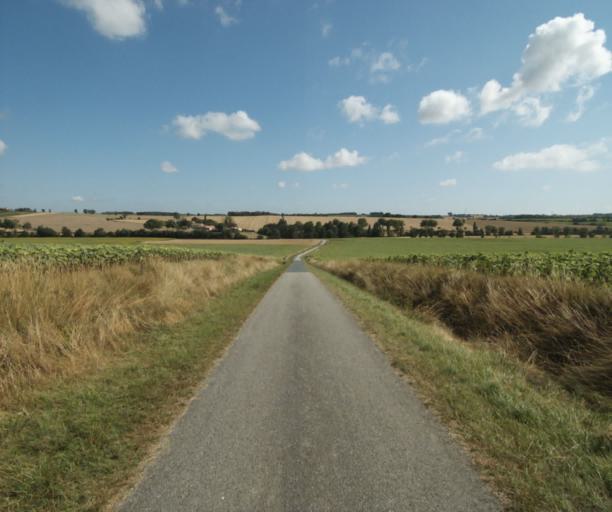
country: FR
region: Midi-Pyrenees
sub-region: Departement de la Haute-Garonne
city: Avignonet-Lauragais
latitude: 43.4412
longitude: 1.7956
